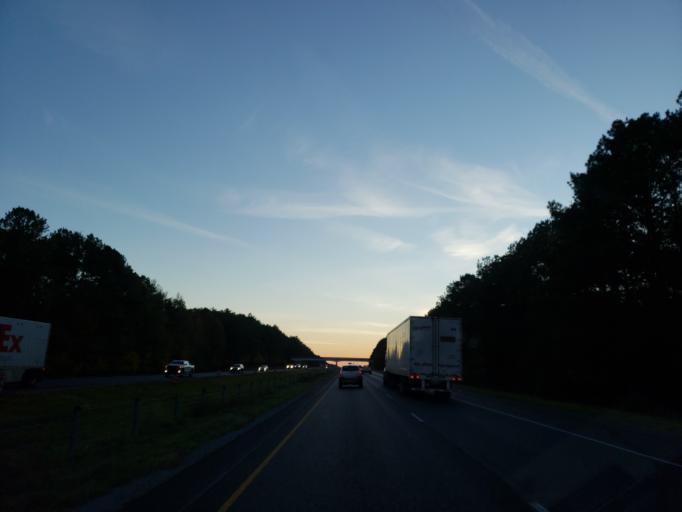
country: US
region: Alabama
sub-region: Sumter County
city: York
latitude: 32.5576
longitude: -88.2631
